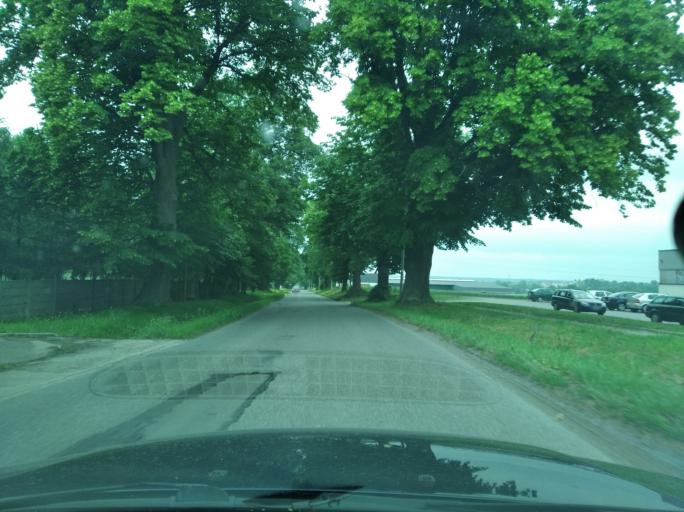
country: PL
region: Subcarpathian Voivodeship
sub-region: Powiat ropczycko-sedziszowski
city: Sedziszow Malopolski
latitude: 50.0573
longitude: 21.6895
